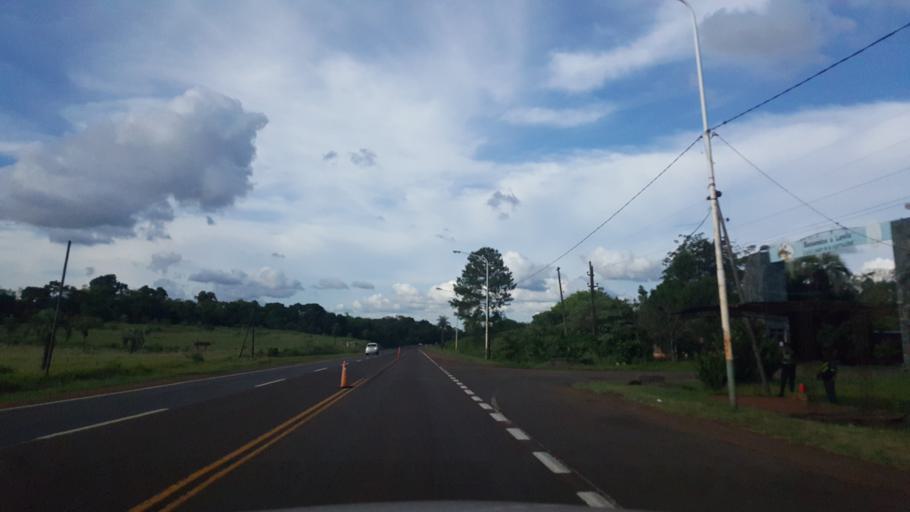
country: AR
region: Misiones
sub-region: Departamento de Candelaria
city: Loreto
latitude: -27.3368
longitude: -55.5444
